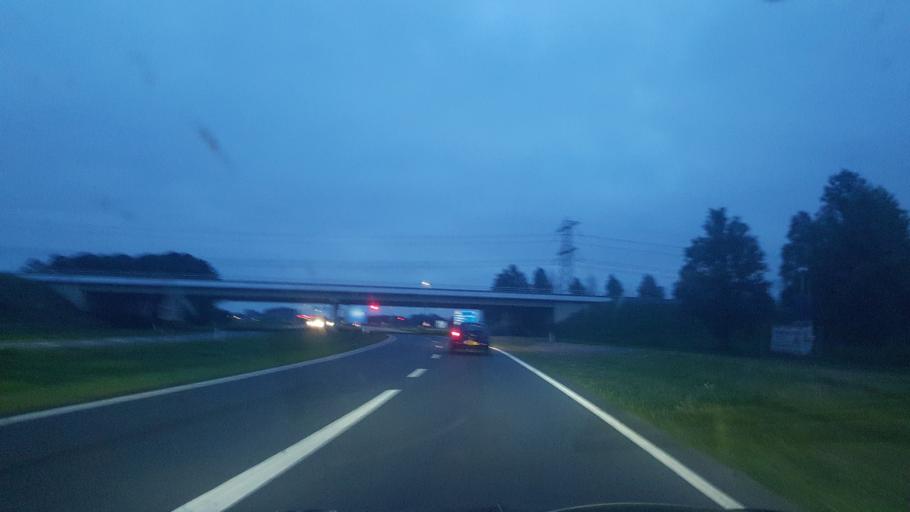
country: NL
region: Friesland
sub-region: Gemeente Boarnsterhim
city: Wergea
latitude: 53.1657
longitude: 5.8309
